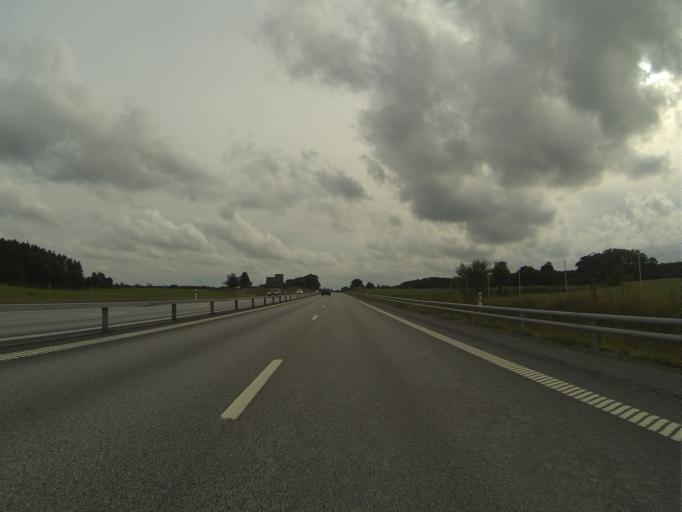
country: SE
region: Skane
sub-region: Horby Kommun
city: Hoerby
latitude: 55.8930
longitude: 13.7211
